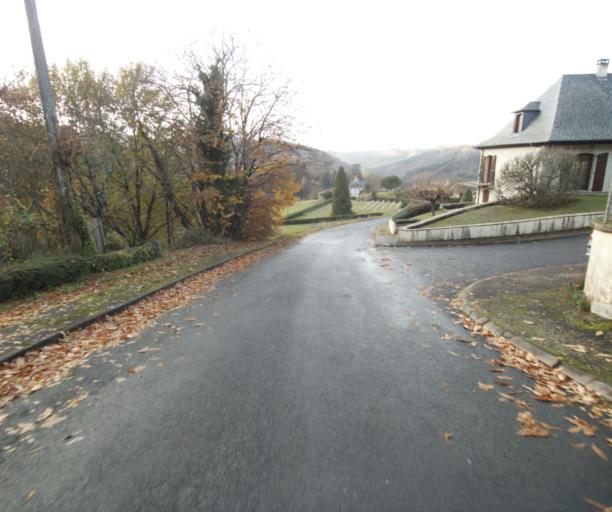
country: FR
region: Limousin
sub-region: Departement de la Correze
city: Cornil
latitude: 45.2061
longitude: 1.6942
